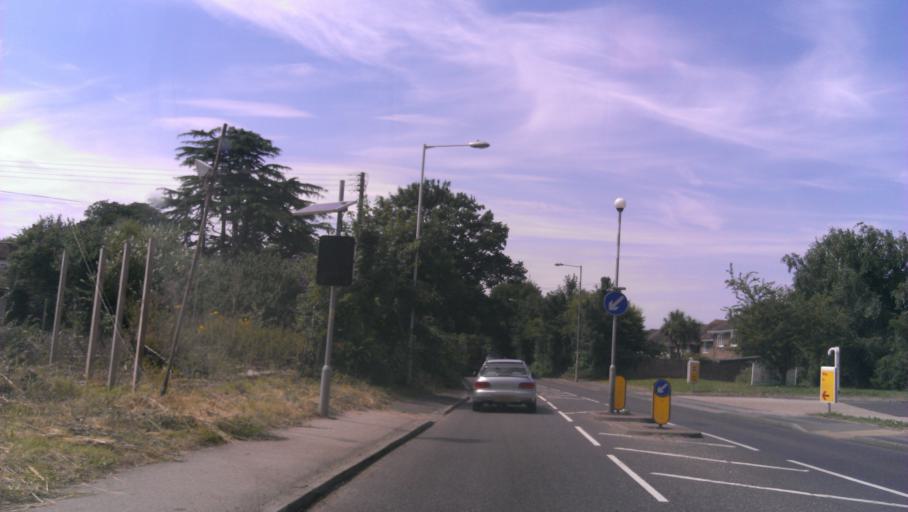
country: GB
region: England
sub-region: Kent
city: Faversham
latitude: 51.3061
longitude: 0.9023
